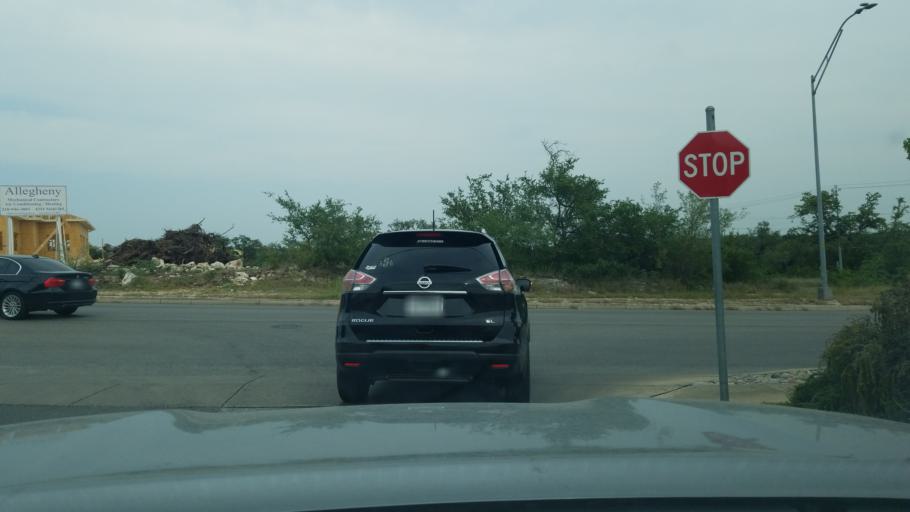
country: US
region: Texas
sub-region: Bexar County
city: Hollywood Park
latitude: 29.6362
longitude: -98.4520
